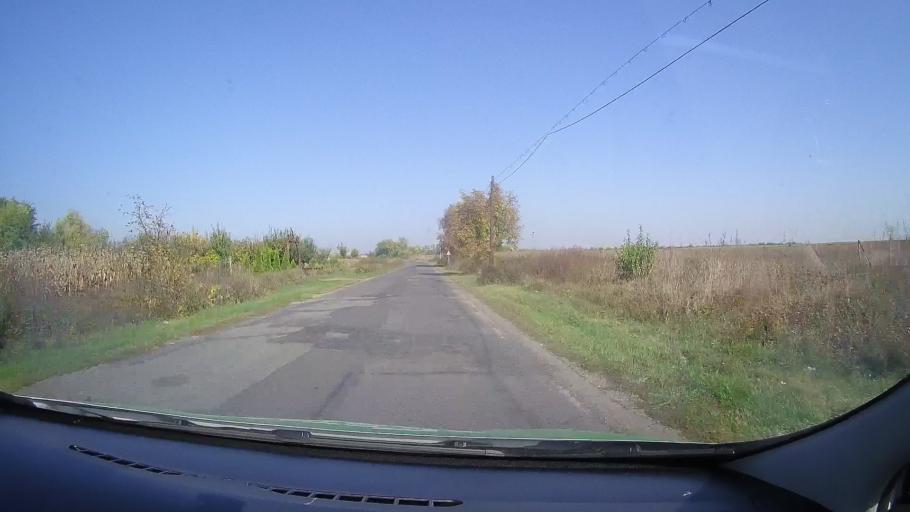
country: RO
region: Satu Mare
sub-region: Comuna Sanislau
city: Sanislau
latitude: 47.6478
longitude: 22.3371
